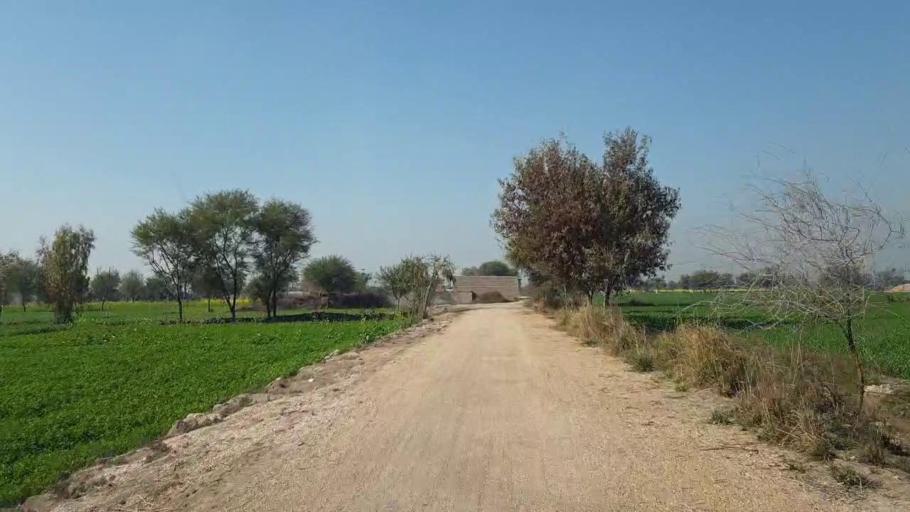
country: PK
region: Sindh
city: Nawabshah
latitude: 26.0587
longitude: 68.4631
